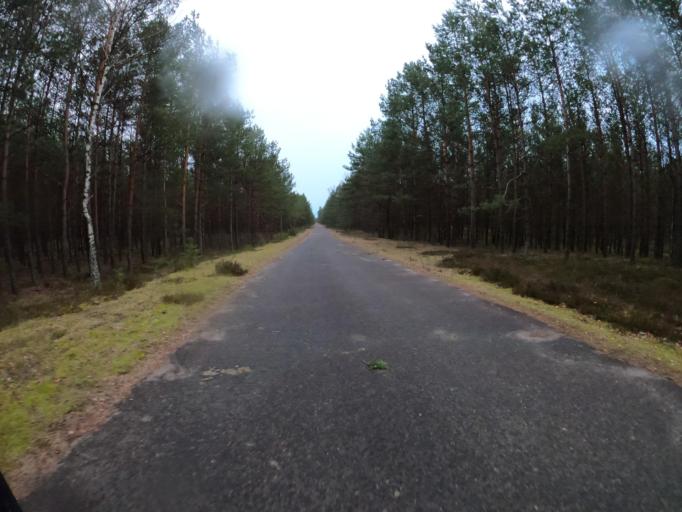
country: PL
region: West Pomeranian Voivodeship
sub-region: Powiat szczecinecki
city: Borne Sulinowo
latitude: 53.5574
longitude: 16.5775
